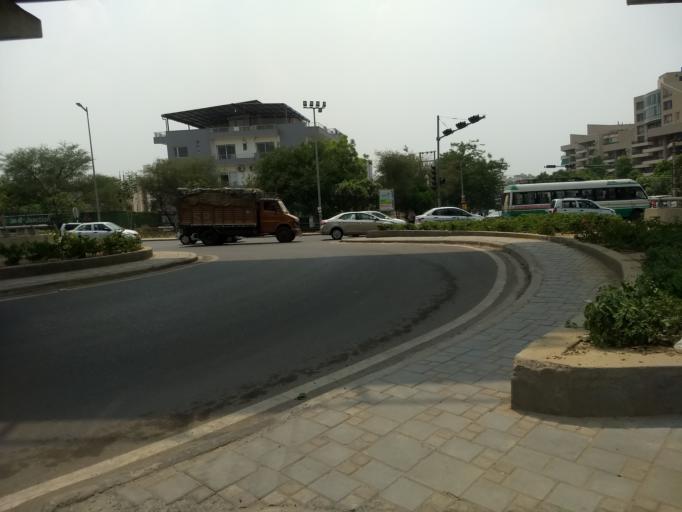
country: IN
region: Haryana
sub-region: Gurgaon
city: Gurgaon
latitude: 28.4679
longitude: 77.0945
